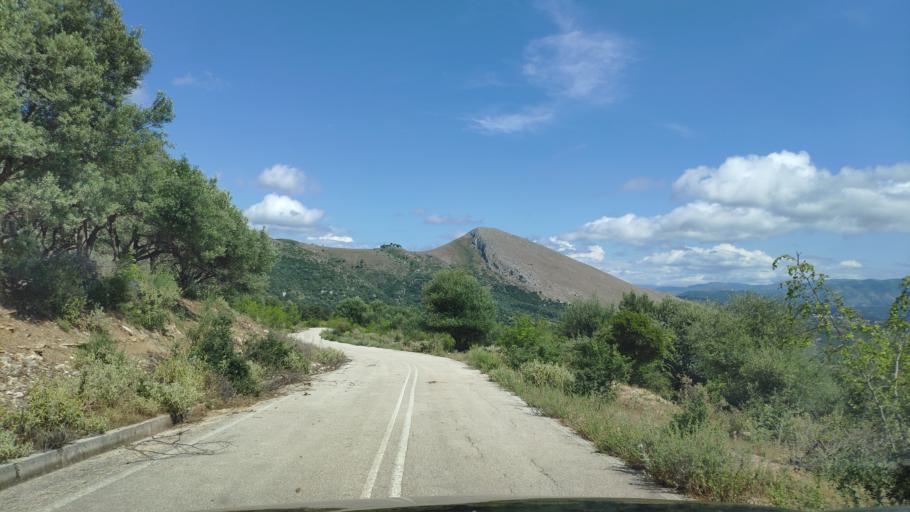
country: AL
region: Vlore
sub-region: Rrethi i Sarandes
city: Konispol
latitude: 39.6320
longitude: 20.2093
